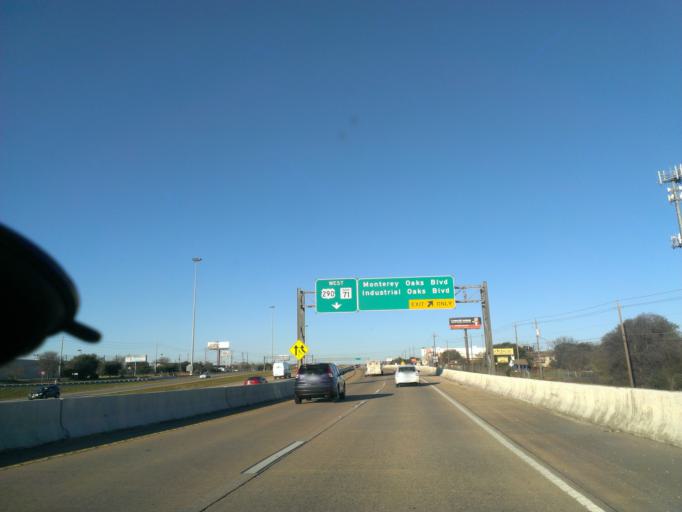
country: US
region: Texas
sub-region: Travis County
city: Rollingwood
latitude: 30.2368
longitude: -97.8280
